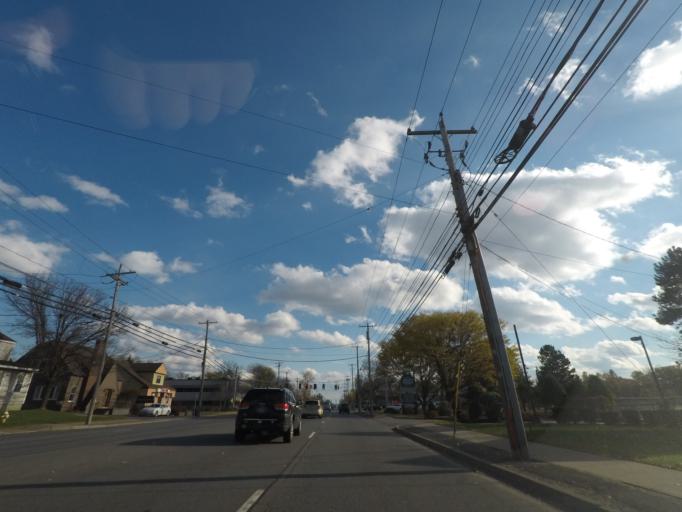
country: US
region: New York
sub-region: Albany County
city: Colonie
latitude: 42.7265
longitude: -73.8431
